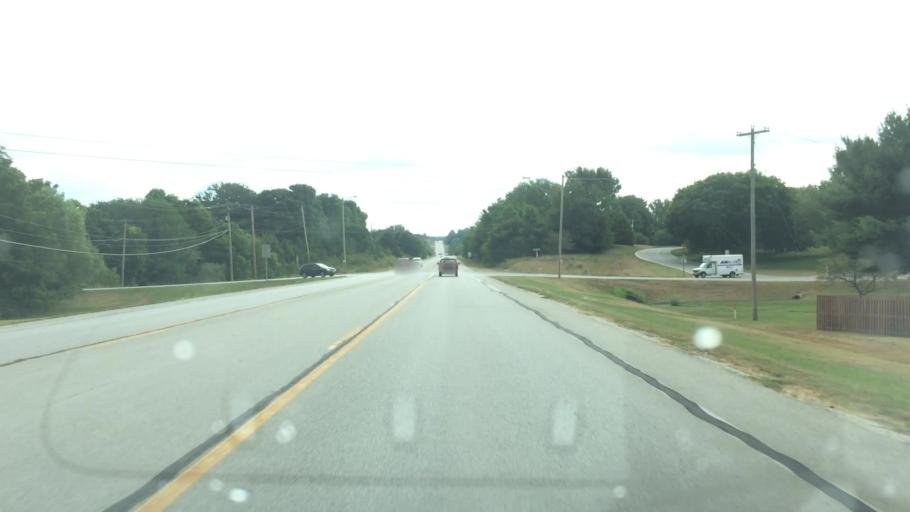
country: US
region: Missouri
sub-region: Greene County
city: Springfield
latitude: 37.1797
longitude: -93.2088
